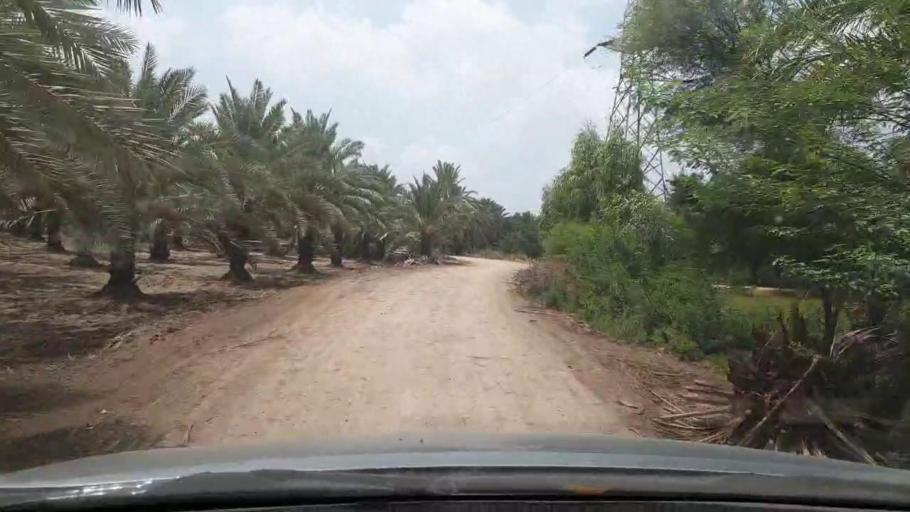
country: PK
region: Sindh
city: Khairpur
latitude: 27.4586
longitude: 68.7192
